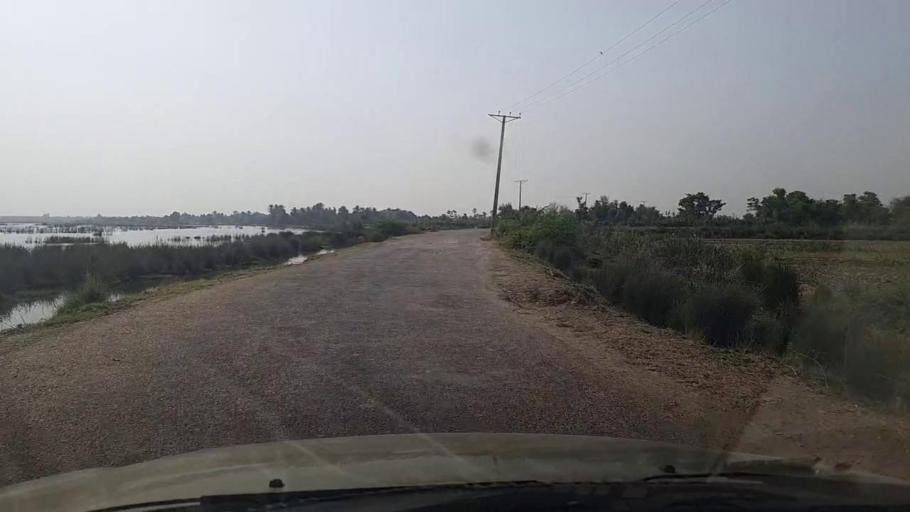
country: PK
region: Sindh
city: Kot Diji
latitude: 27.2836
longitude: 68.6496
